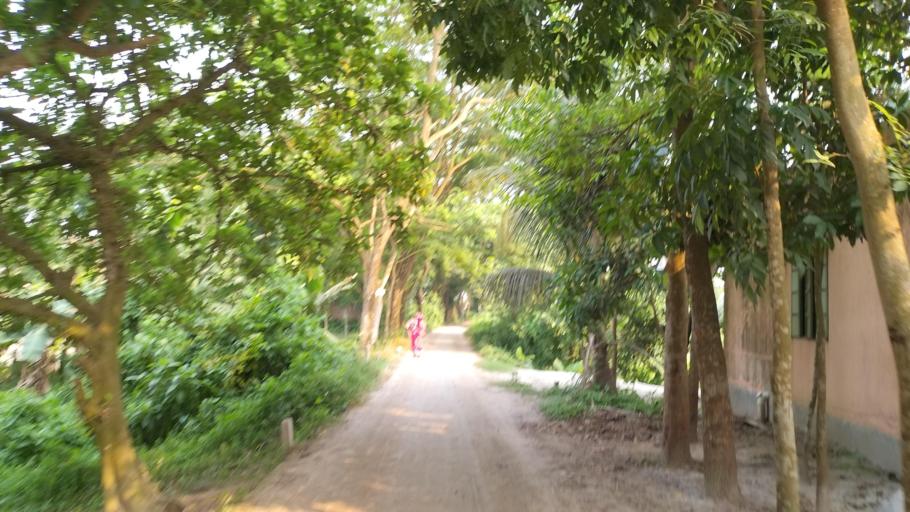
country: BD
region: Dhaka
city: Azimpur
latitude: 23.6733
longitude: 90.3124
